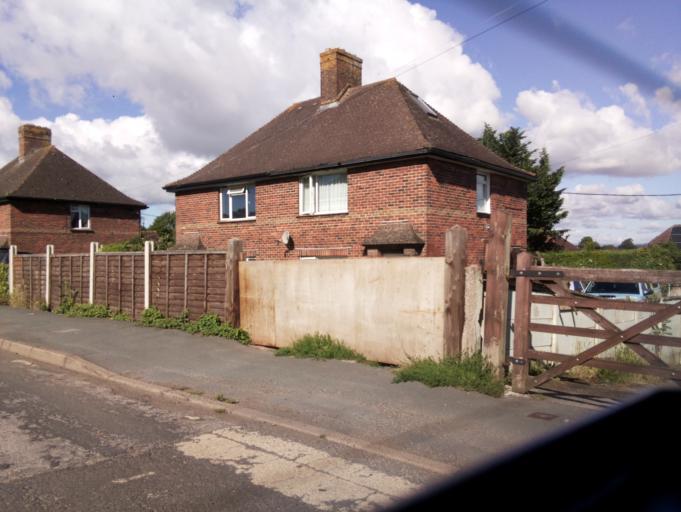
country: GB
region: England
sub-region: Herefordshire
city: Walford
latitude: 51.9030
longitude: -2.5888
